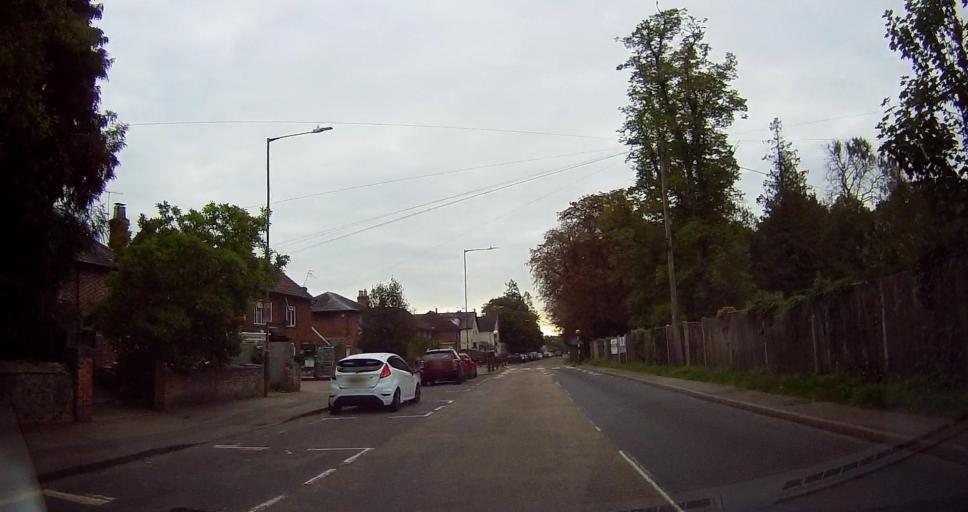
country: GB
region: England
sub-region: Kent
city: Tonbridge
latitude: 51.2171
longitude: 0.2390
